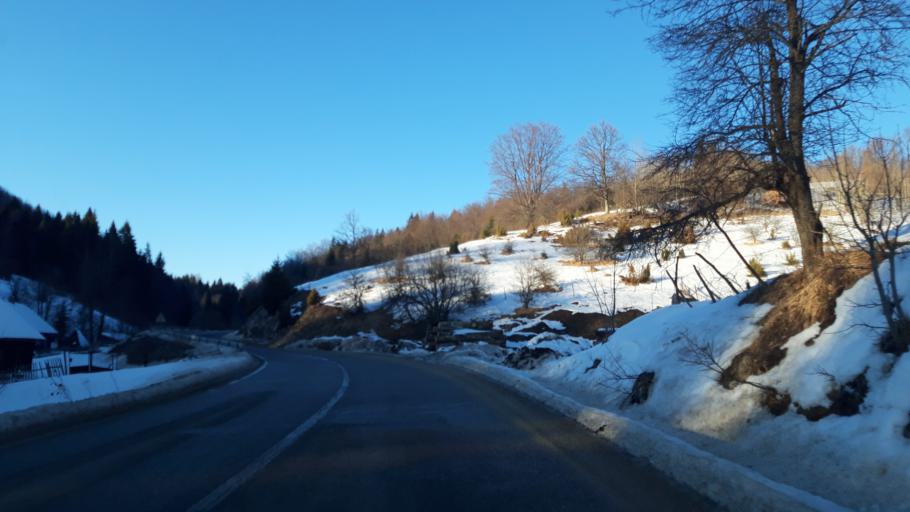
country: BA
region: Republika Srpska
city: Han Pijesak
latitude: 44.1263
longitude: 18.9627
